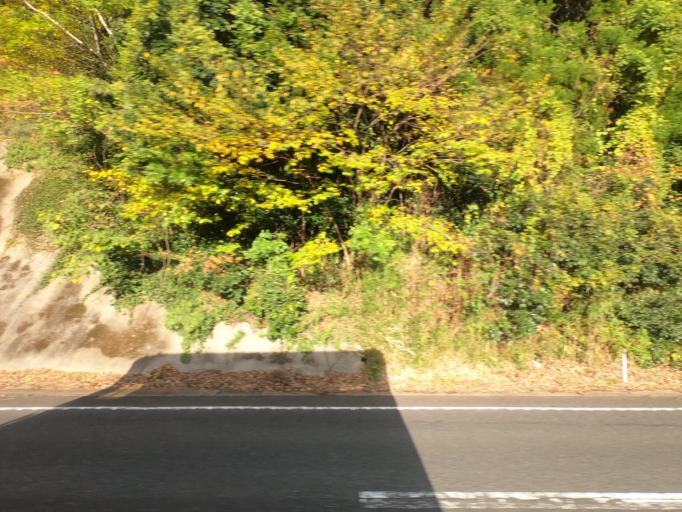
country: JP
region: Kumamoto
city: Minamata
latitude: 32.2445
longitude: 130.4786
